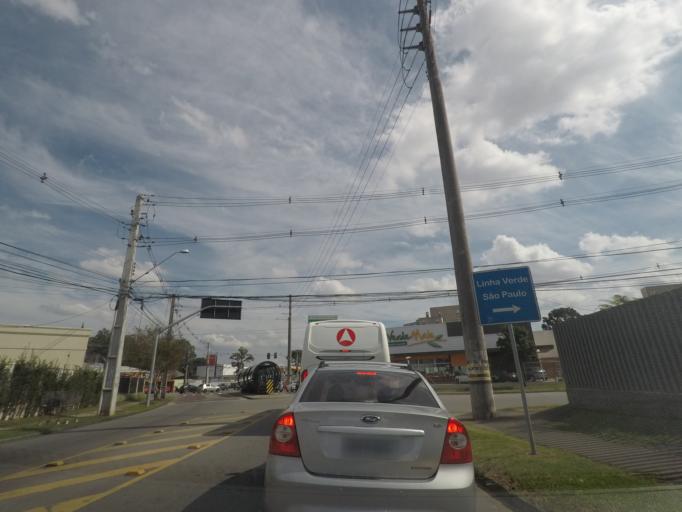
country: BR
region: Parana
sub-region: Curitiba
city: Curitiba
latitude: -25.4960
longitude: -49.2700
